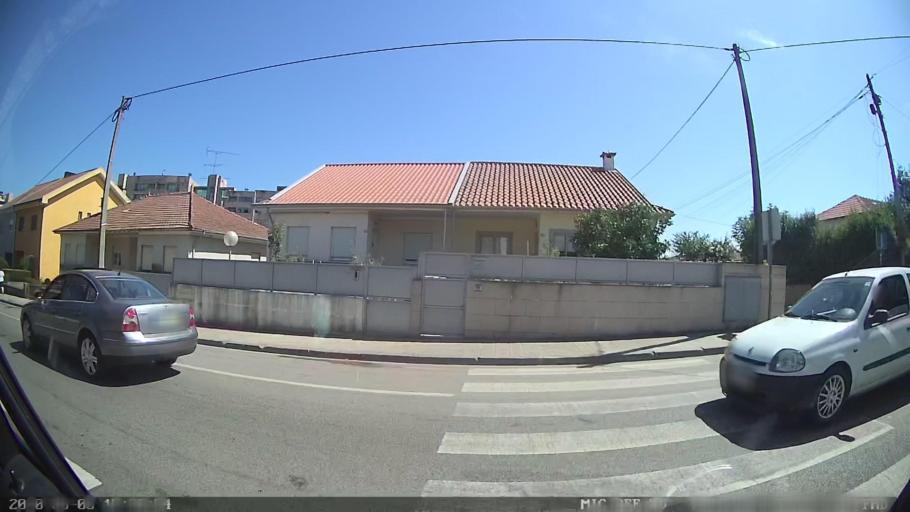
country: PT
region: Porto
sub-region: Gondomar
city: Baguim do Monte
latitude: 41.2046
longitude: -8.5517
